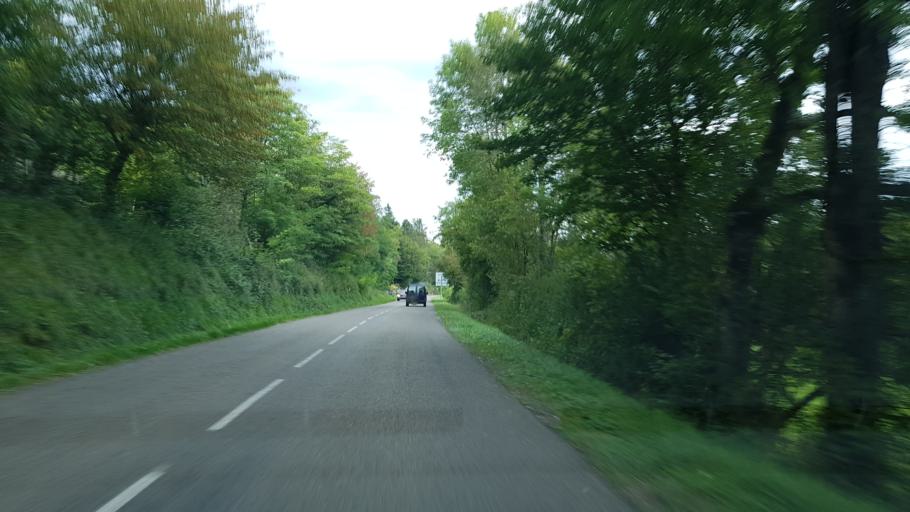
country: FR
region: Rhone-Alpes
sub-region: Departement de l'Ain
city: Cuisiat
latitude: 46.2435
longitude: 5.4228
